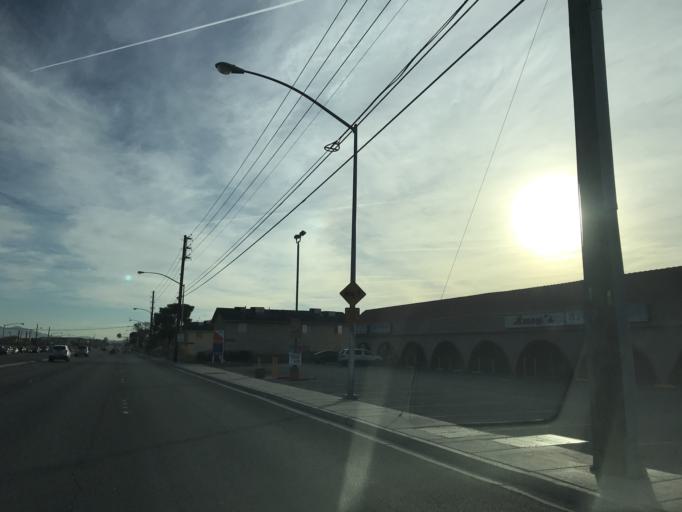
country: US
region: Nevada
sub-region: Clark County
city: Nellis Air Force Base
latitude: 36.2403
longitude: -115.0709
